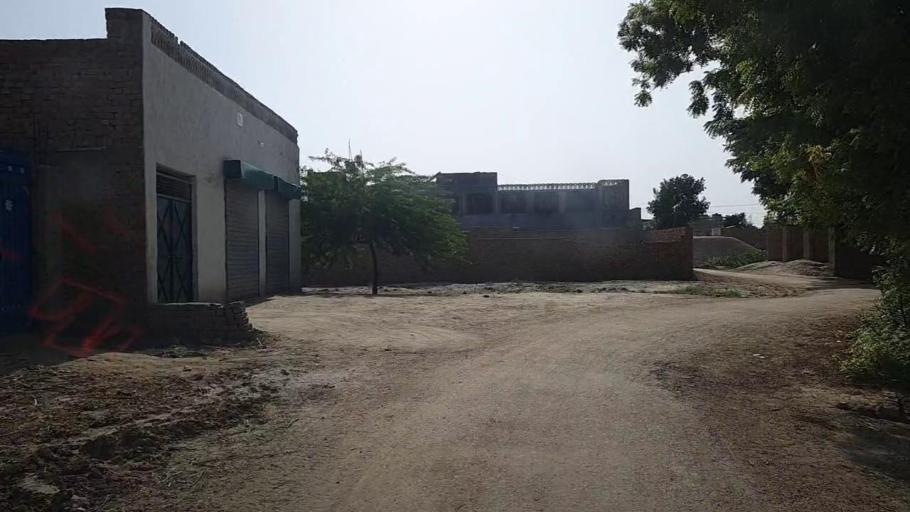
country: PK
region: Sindh
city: Karaundi
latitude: 26.8588
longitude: 68.3612
